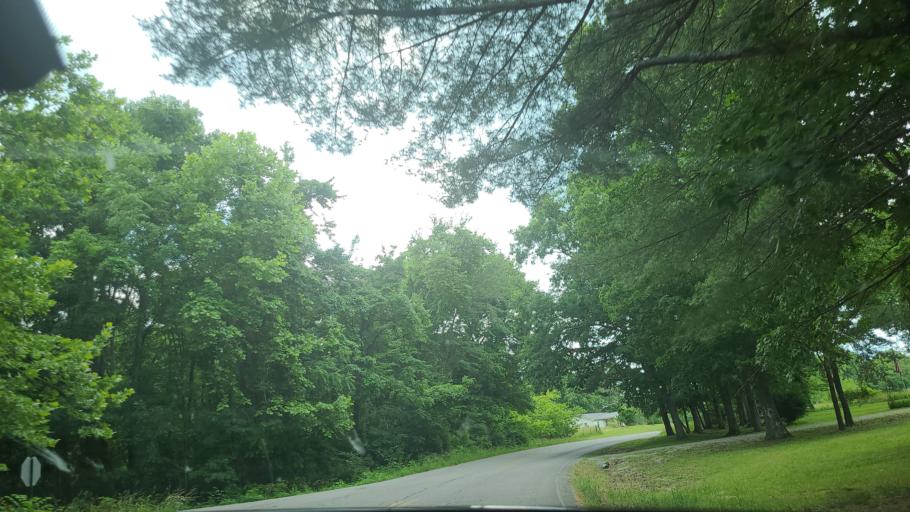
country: US
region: Tennessee
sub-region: Cumberland County
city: Lake Tansi
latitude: 35.7859
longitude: -85.0537
